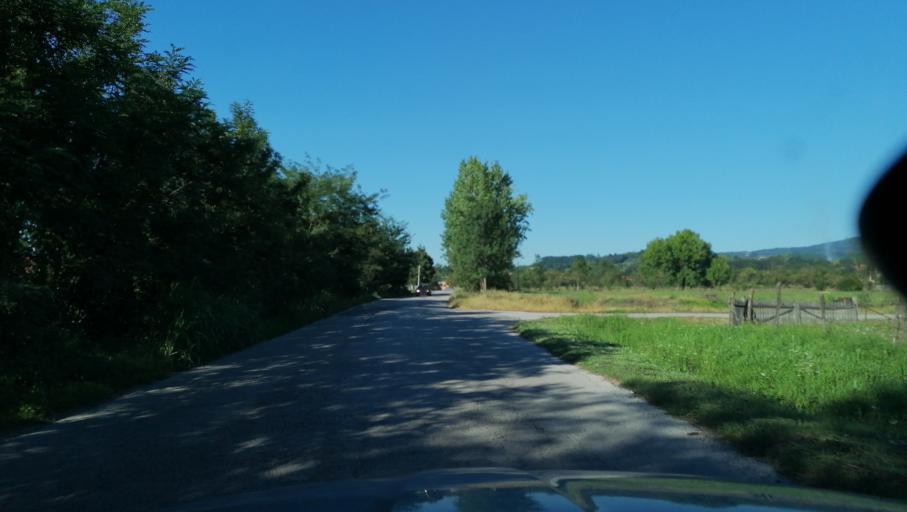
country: RS
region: Central Serbia
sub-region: Raski Okrug
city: Kraljevo
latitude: 43.8399
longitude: 20.5990
